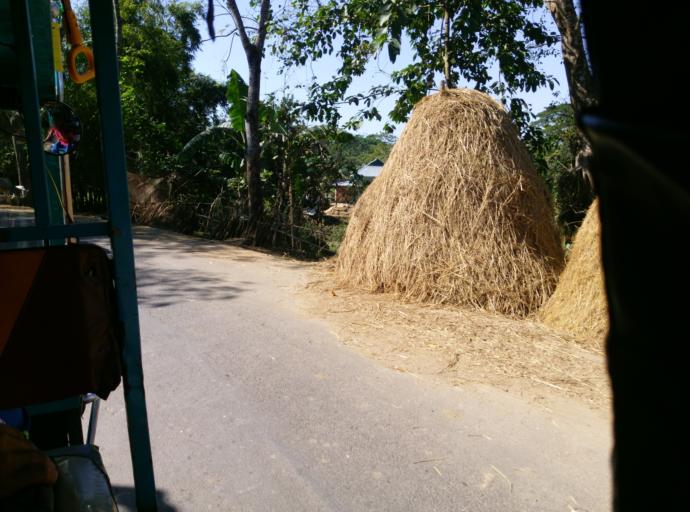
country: BD
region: Dhaka
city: Netrakona
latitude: 25.0683
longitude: 90.5018
